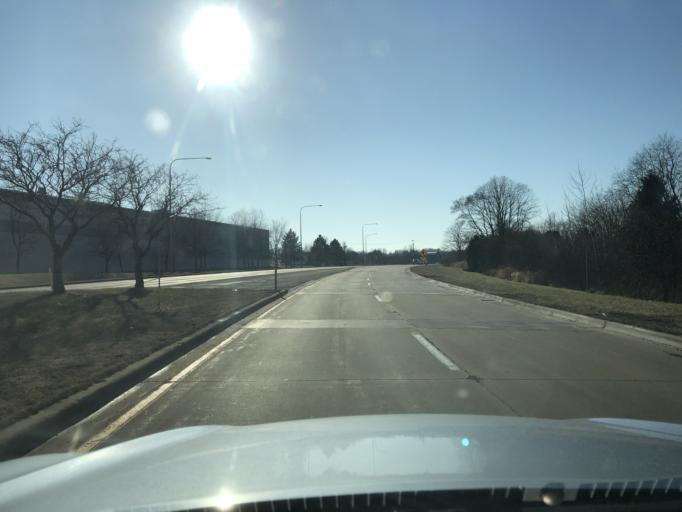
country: US
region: Illinois
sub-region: DuPage County
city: Roselle
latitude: 41.9906
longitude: -88.0471
